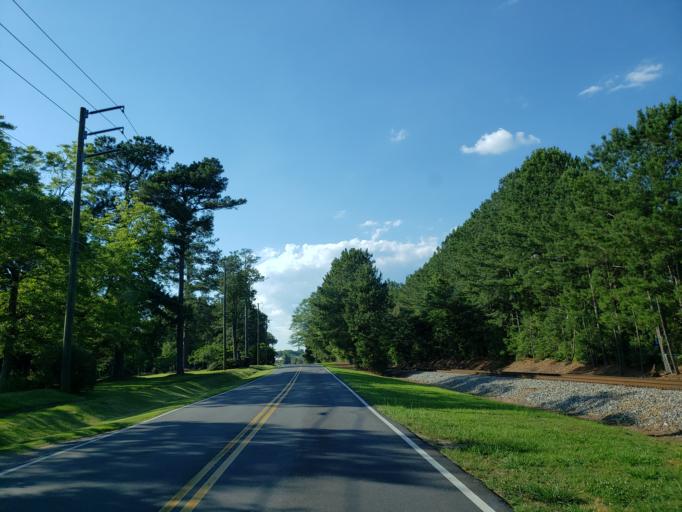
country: US
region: Georgia
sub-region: Haralson County
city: Bremen
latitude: 33.7107
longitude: -85.1444
